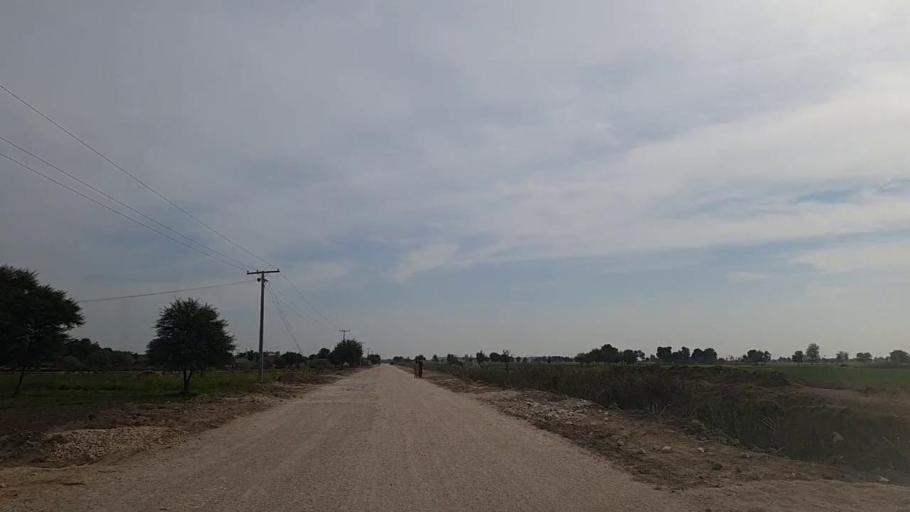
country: PK
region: Sindh
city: Daur
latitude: 26.4143
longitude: 68.4897
